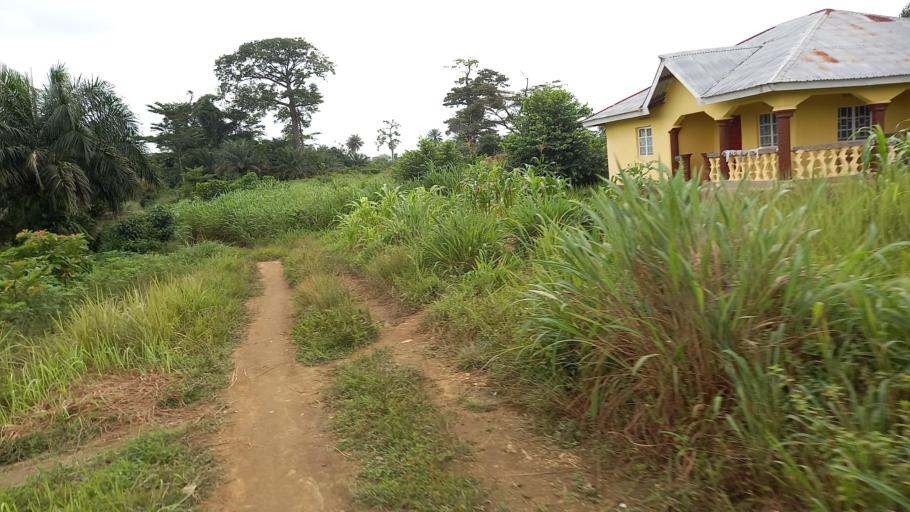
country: SL
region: Eastern Province
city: Kailahun
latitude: 8.2907
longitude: -10.5696
